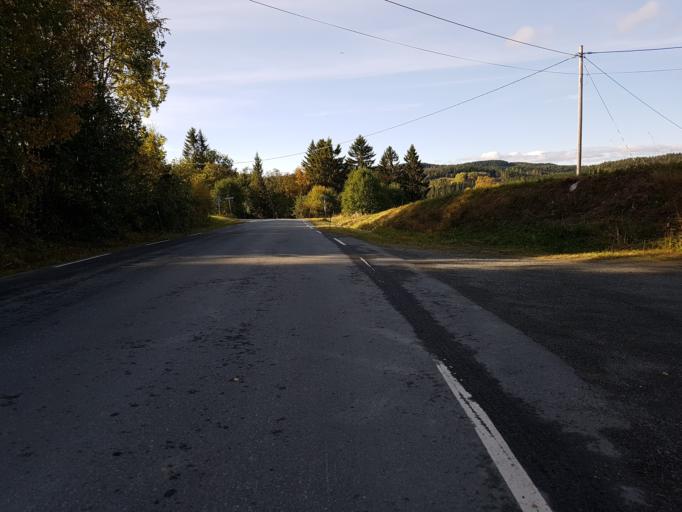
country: NO
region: Sor-Trondelag
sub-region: Klaebu
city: Klaebu
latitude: 63.3402
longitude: 10.5690
